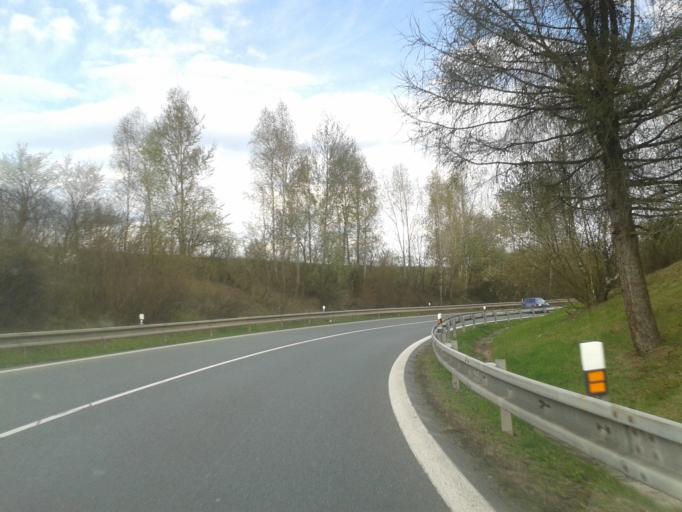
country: CZ
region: Central Bohemia
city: Rudna
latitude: 50.0251
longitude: 14.2029
